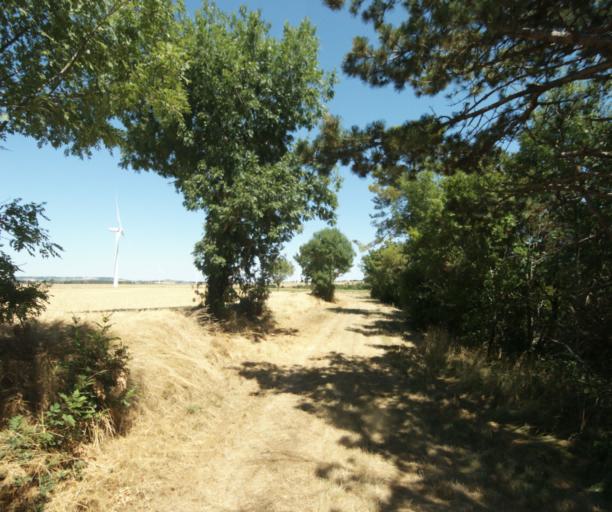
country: FR
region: Midi-Pyrenees
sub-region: Departement de la Haute-Garonne
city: Saint-Felix-Lauragais
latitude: 43.4548
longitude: 1.9078
